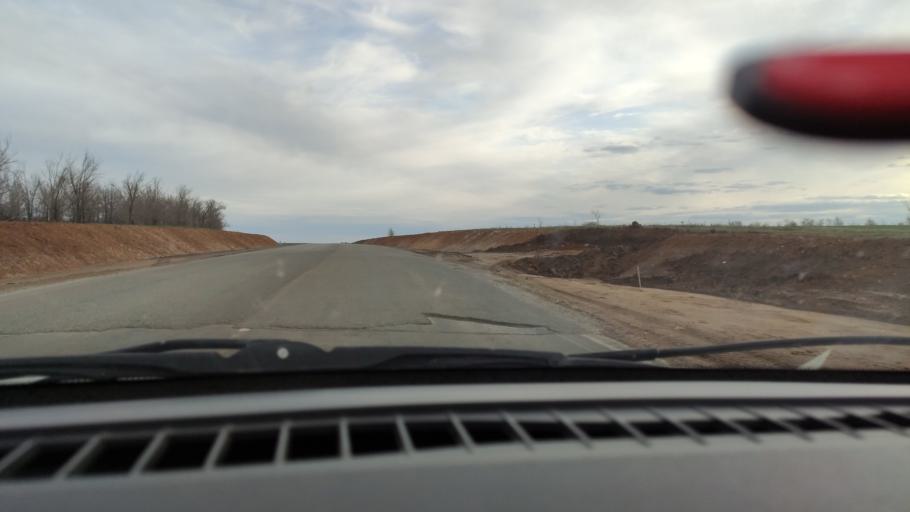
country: RU
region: Orenburg
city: Sakmara
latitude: 52.1822
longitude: 55.2929
